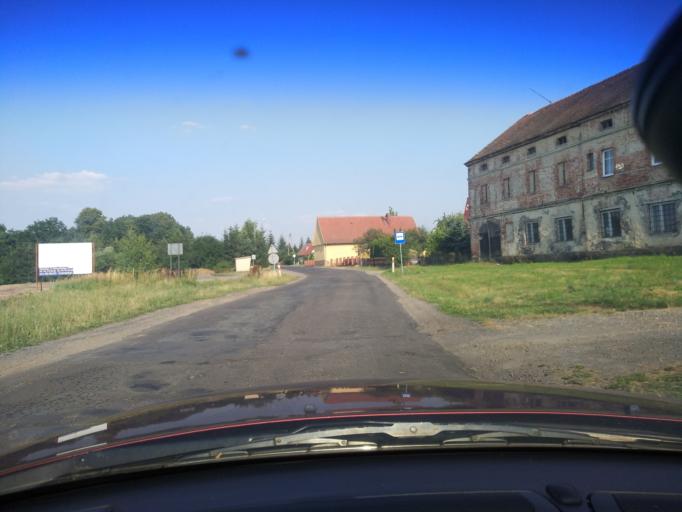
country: PL
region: Lower Silesian Voivodeship
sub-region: Powiat zgorzelecki
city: Sulikow
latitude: 51.0791
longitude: 15.1145
